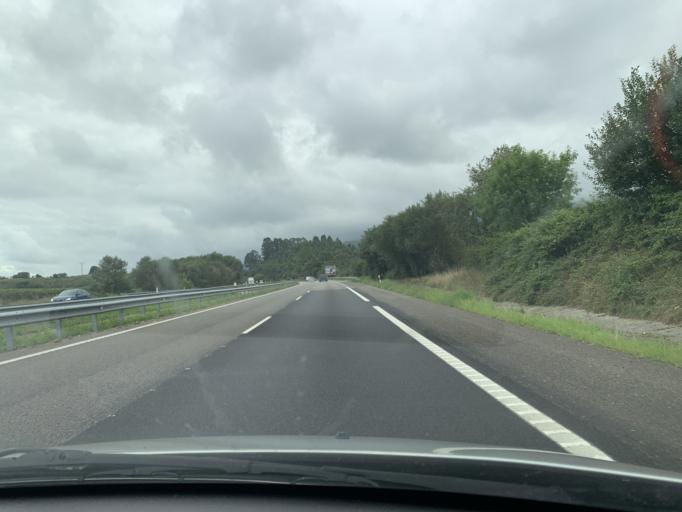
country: ES
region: Asturias
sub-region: Province of Asturias
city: Llanes
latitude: 43.4150
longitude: -4.7875
